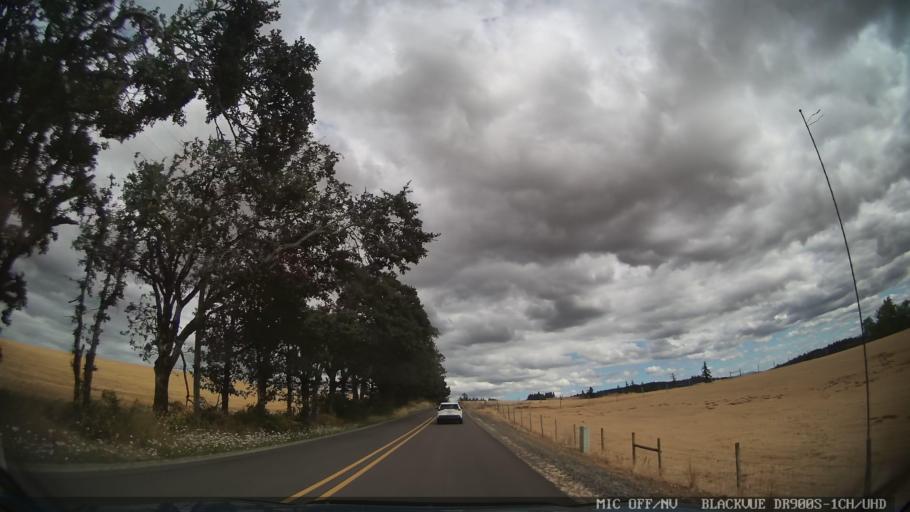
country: US
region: Oregon
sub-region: Marion County
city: Sublimity
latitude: 44.8678
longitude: -122.7537
